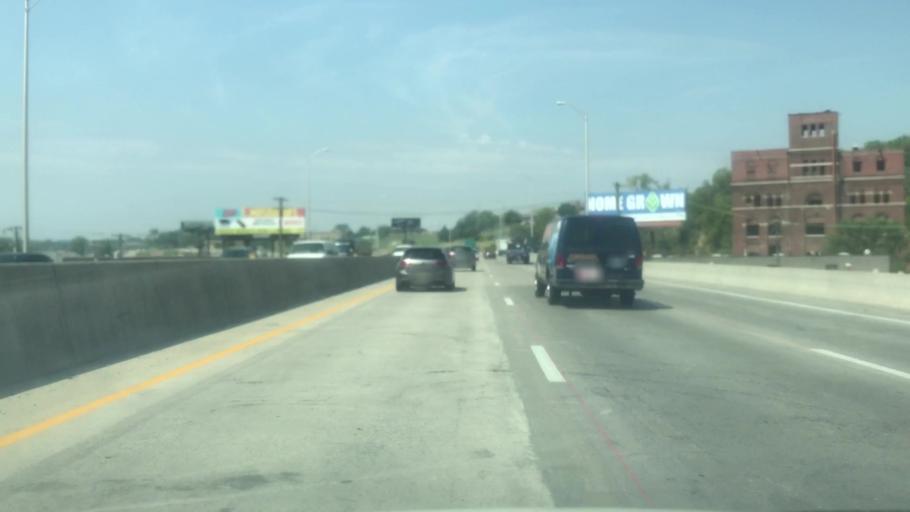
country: US
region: Missouri
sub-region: Jackson County
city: Kansas City
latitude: 39.0759
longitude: -94.6014
